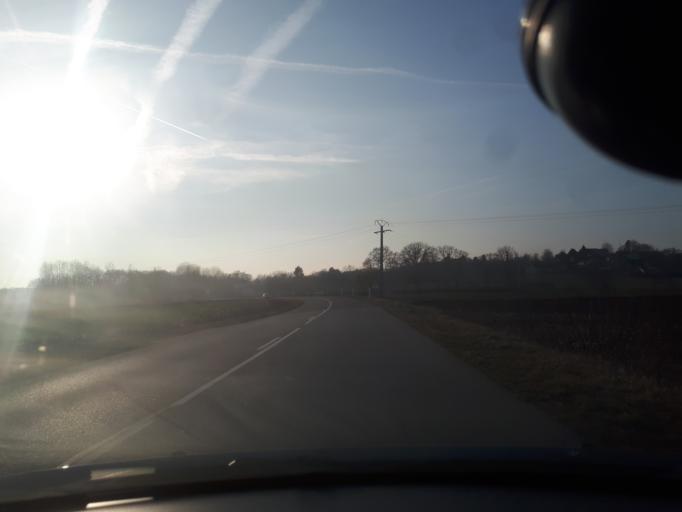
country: FR
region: Rhone-Alpes
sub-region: Departement de l'Isere
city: Morestel
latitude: 45.6900
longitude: 5.5090
